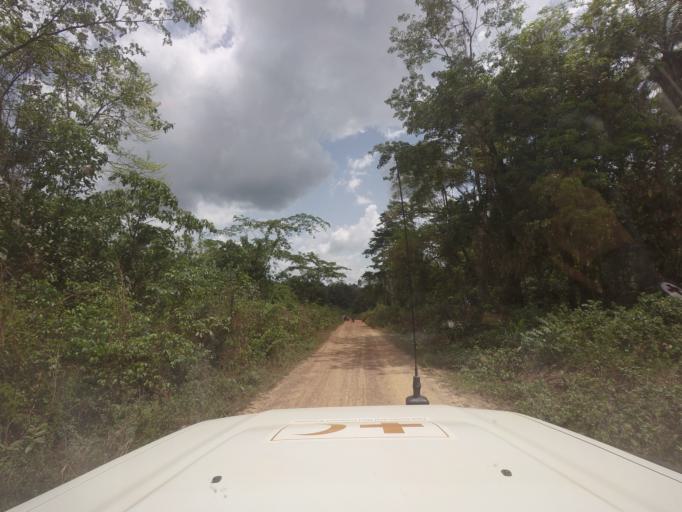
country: LR
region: Bong
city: Gbarnga
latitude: 7.0574
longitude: -9.2385
